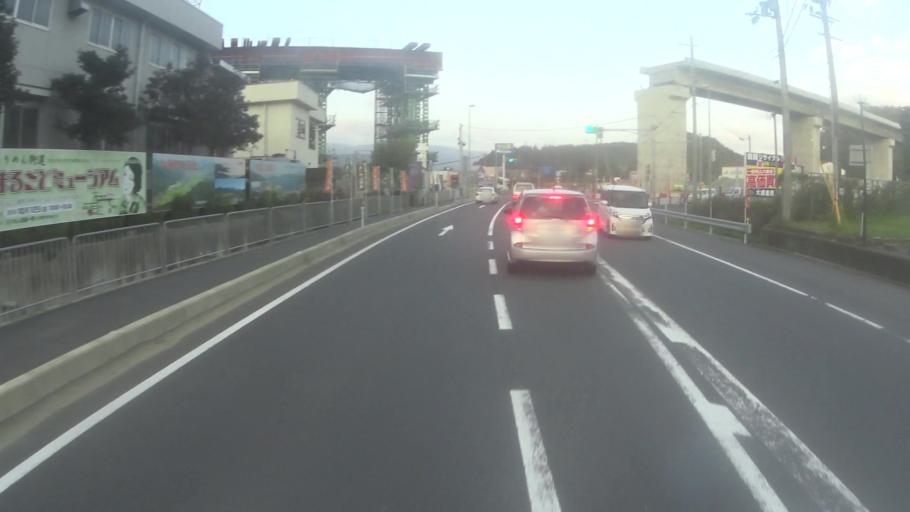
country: JP
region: Kyoto
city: Miyazu
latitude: 35.5507
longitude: 135.1387
